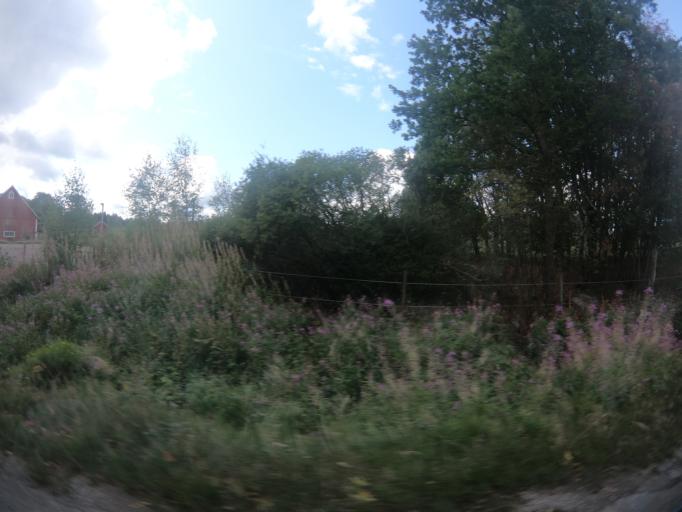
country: SE
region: Kronoberg
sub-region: Vaxjo Kommun
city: Braas
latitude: 57.1519
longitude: 14.9639
